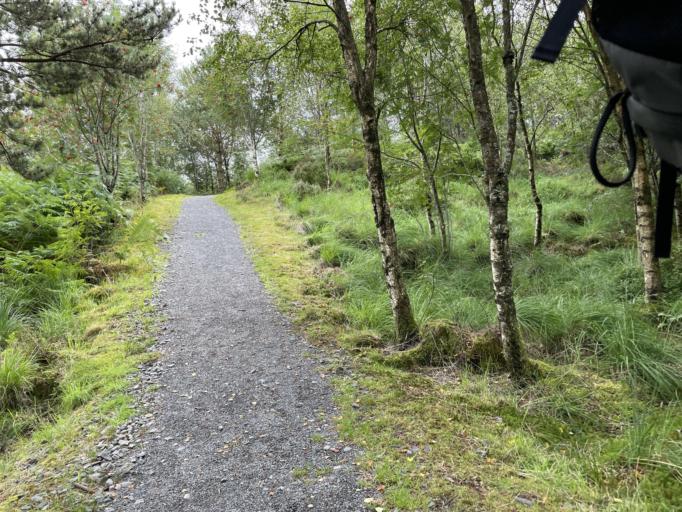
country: GB
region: Scotland
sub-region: Dumfries and Galloway
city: Newton Stewart
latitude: 55.0817
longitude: -4.5089
